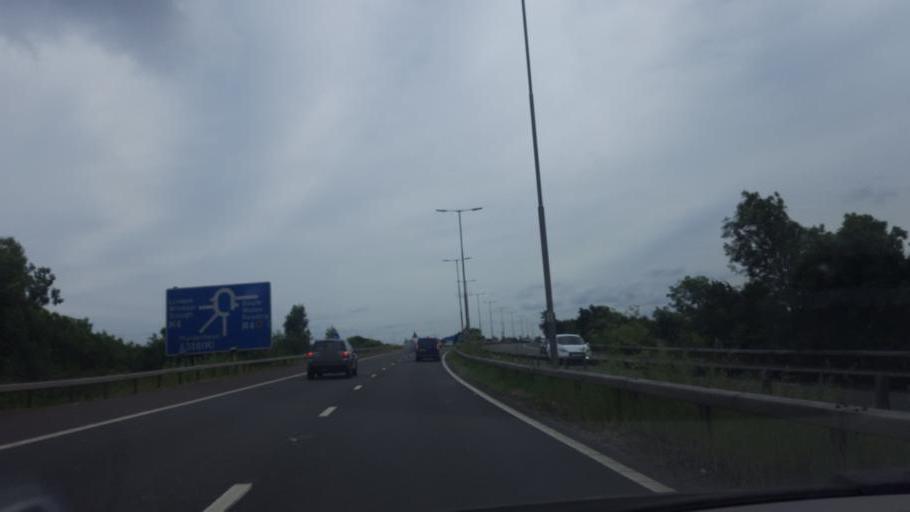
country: GB
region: England
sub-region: Royal Borough of Windsor and Maidenhead
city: Maidenhead
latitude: 51.5029
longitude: -0.7272
